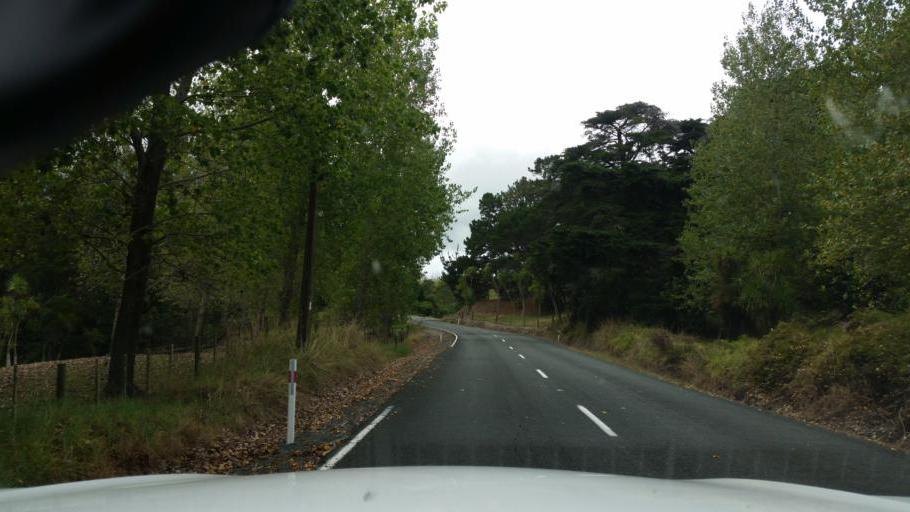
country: NZ
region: Auckland
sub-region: Auckland
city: Wellsford
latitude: -36.1539
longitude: 174.2562
